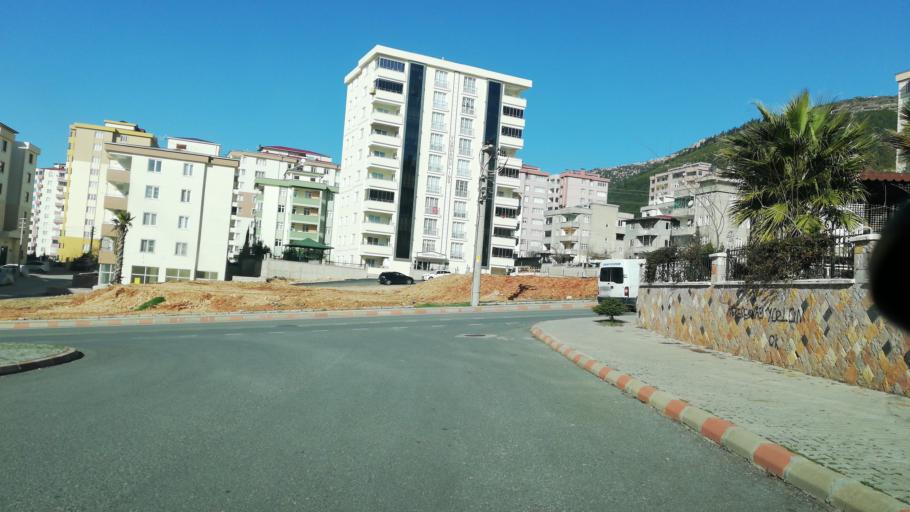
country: TR
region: Kahramanmaras
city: Kahramanmaras
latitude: 37.5994
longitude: 36.8841
